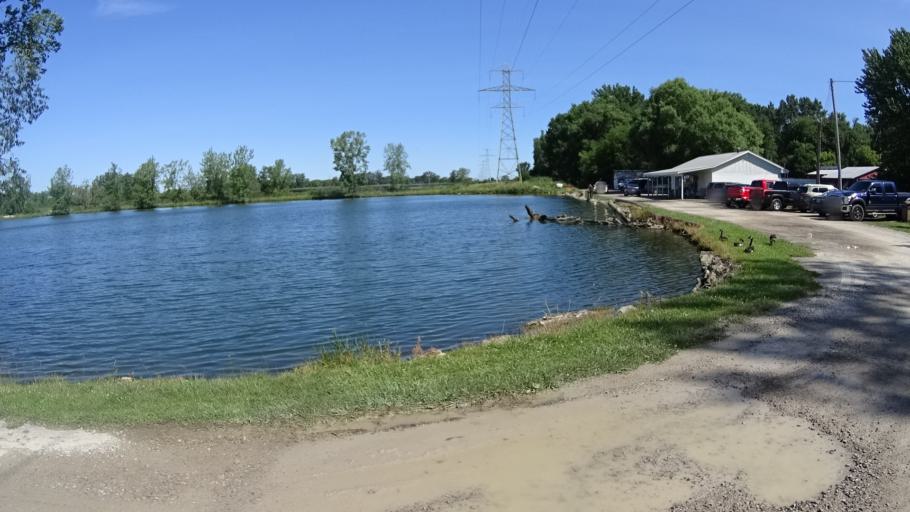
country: US
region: Ohio
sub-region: Erie County
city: Sandusky
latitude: 41.4521
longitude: -82.8083
